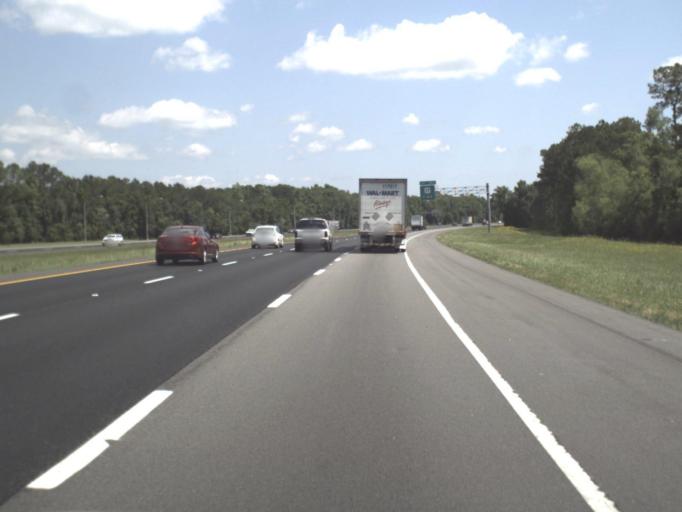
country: US
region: Florida
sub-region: Nassau County
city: Yulee
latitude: 30.6969
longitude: -81.6764
